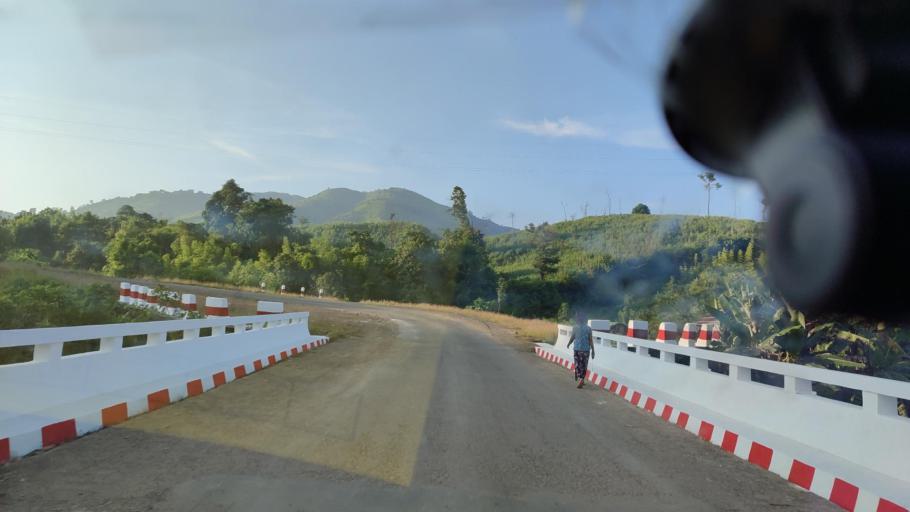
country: MM
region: Magway
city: Minbu
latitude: 19.8614
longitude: 94.1386
